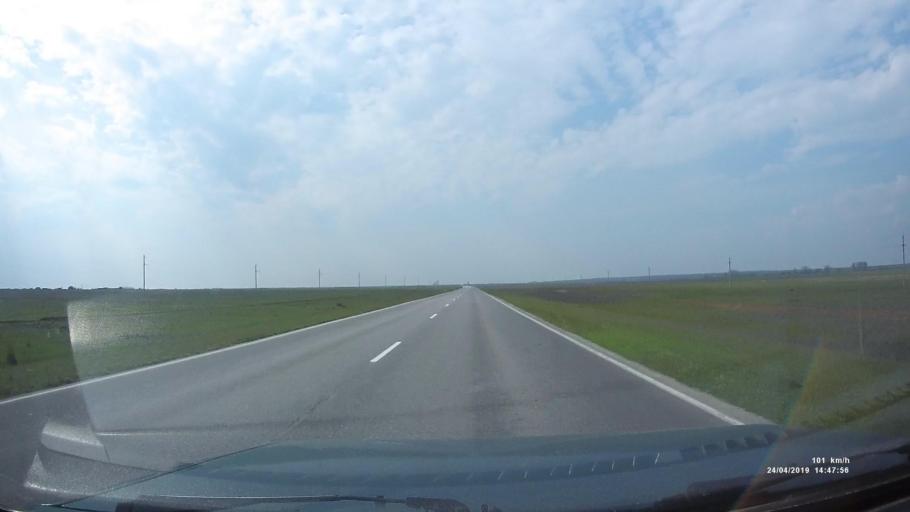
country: RU
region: Rostov
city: Remontnoye
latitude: 46.4963
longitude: 43.7644
